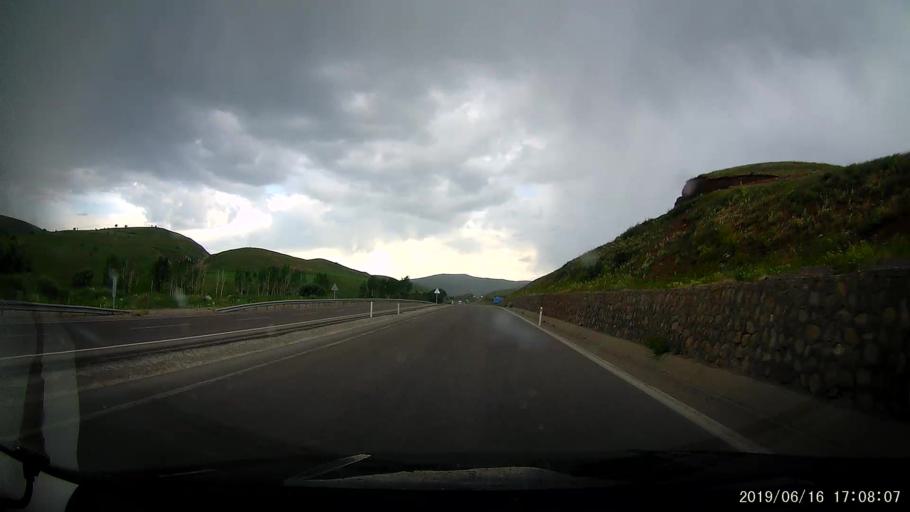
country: TR
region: Erzurum
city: Askale
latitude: 39.9134
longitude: 40.6648
